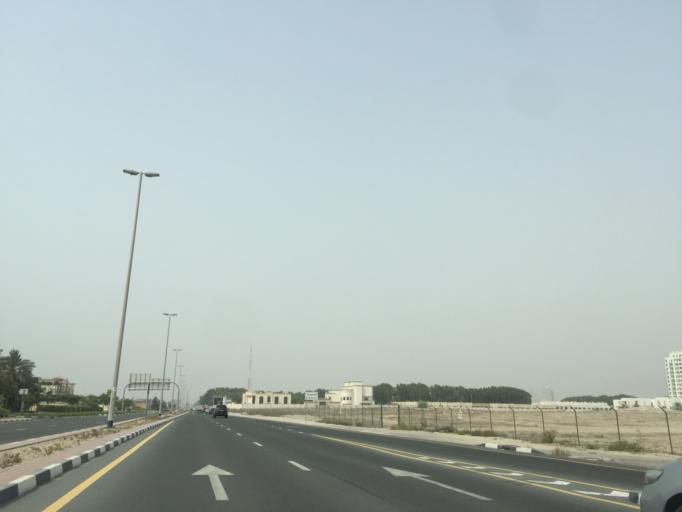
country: AE
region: Dubai
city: Dubai
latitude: 25.1116
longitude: 55.1737
